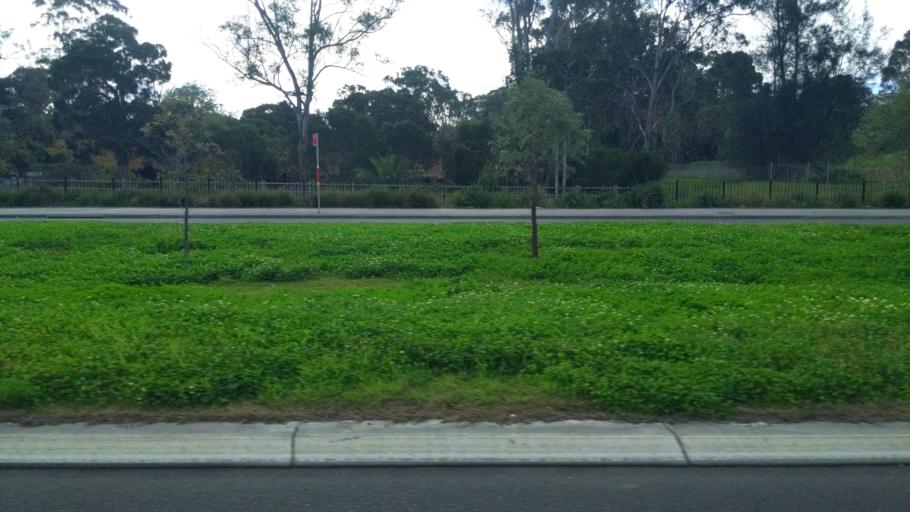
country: AU
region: New South Wales
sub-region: Blacktown
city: Riverstone
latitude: -33.7054
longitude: 150.8492
